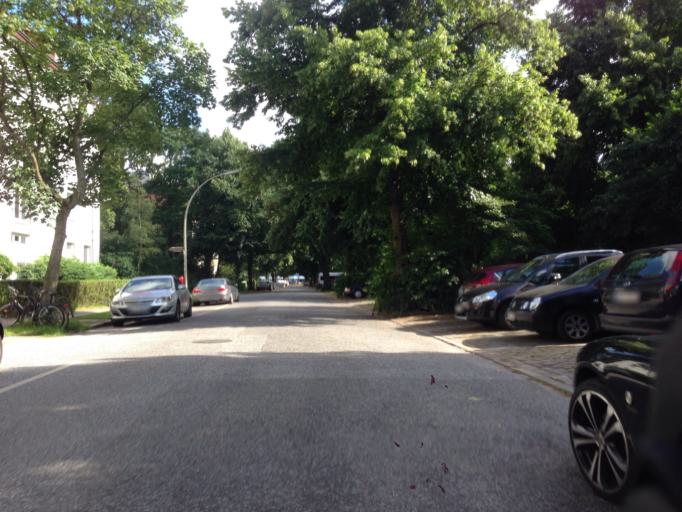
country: DE
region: Hamburg
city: Hamburg
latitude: 53.5777
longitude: 10.0349
